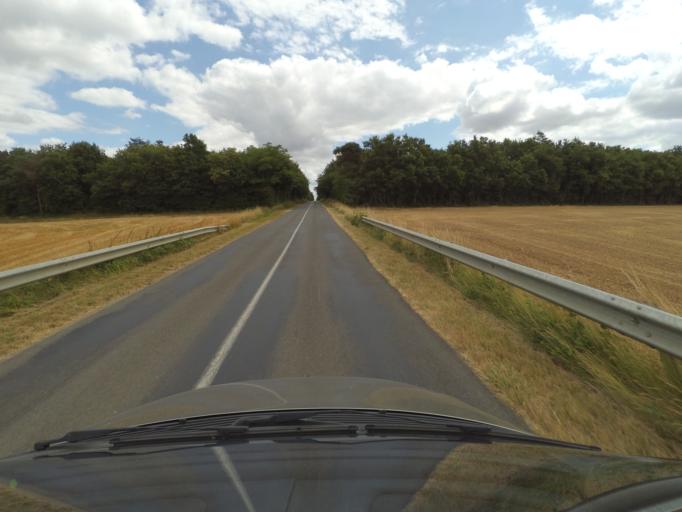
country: FR
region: Poitou-Charentes
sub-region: Departement de la Vienne
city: Saint-Savin
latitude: 46.5603
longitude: 0.9054
